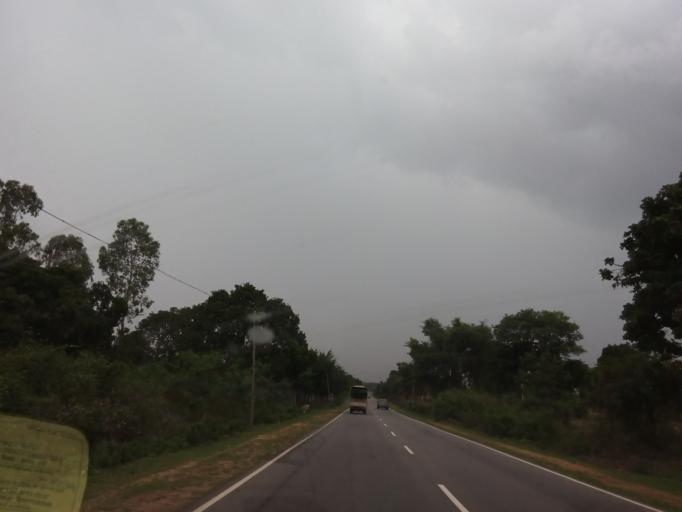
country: IN
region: Karnataka
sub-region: Hassan
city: Hassan
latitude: 13.1042
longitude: 76.0205
